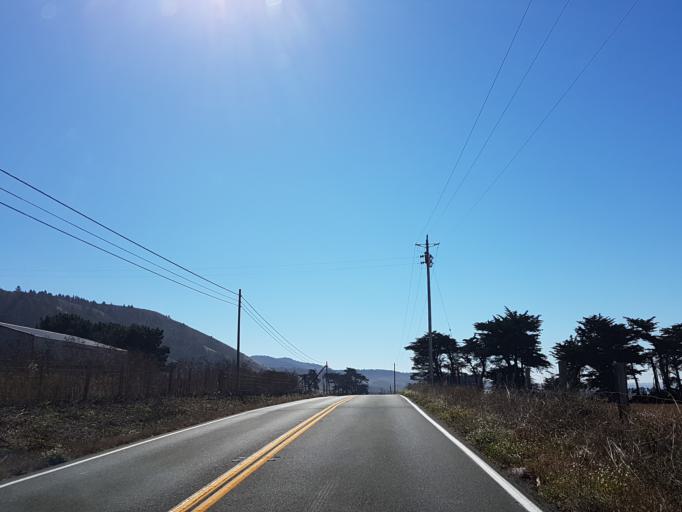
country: US
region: California
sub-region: Mendocino County
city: Boonville
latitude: 39.0822
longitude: -123.6973
